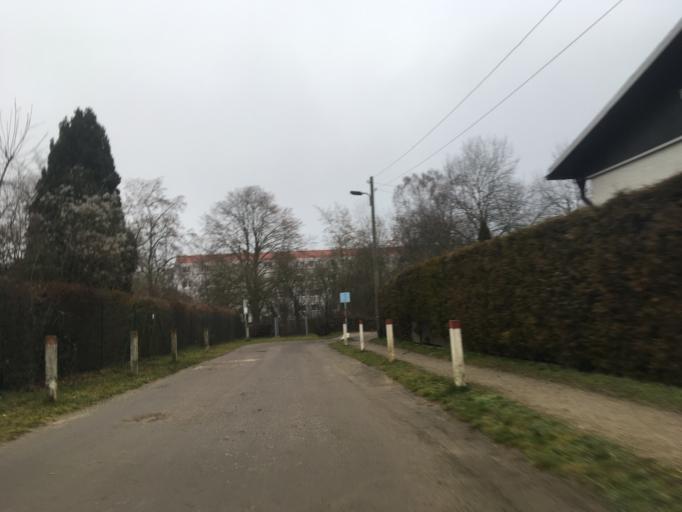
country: DE
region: Berlin
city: Buch
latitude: 52.6231
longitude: 13.4976
